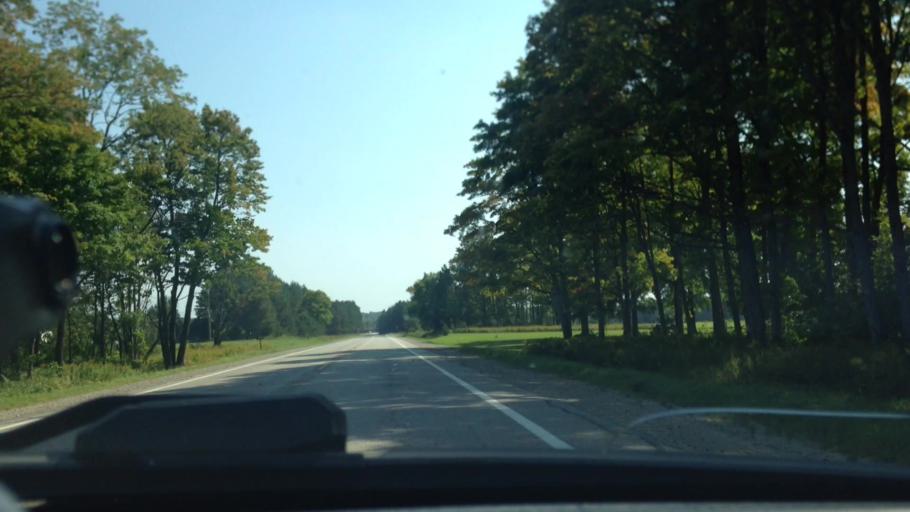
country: US
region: Michigan
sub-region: Luce County
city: Newberry
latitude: 46.3186
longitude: -85.6659
